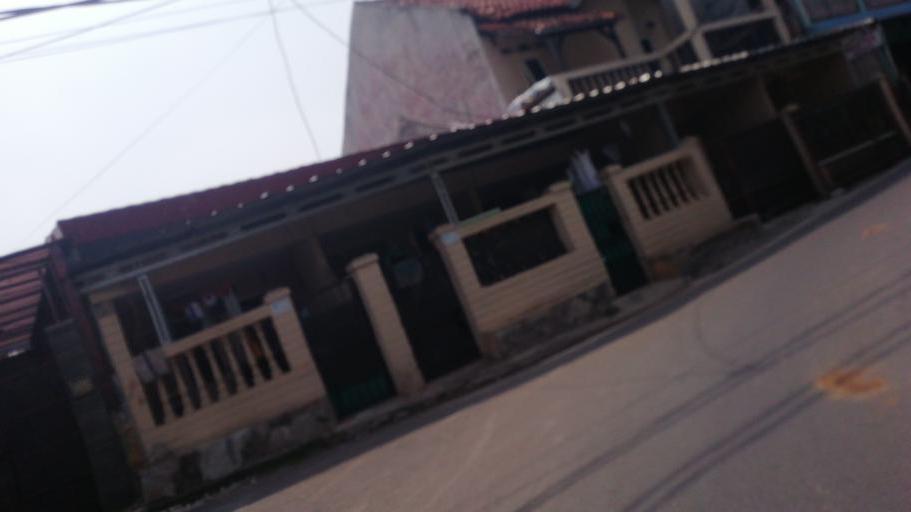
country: ID
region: West Java
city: Depok
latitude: -6.3511
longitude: 106.7978
